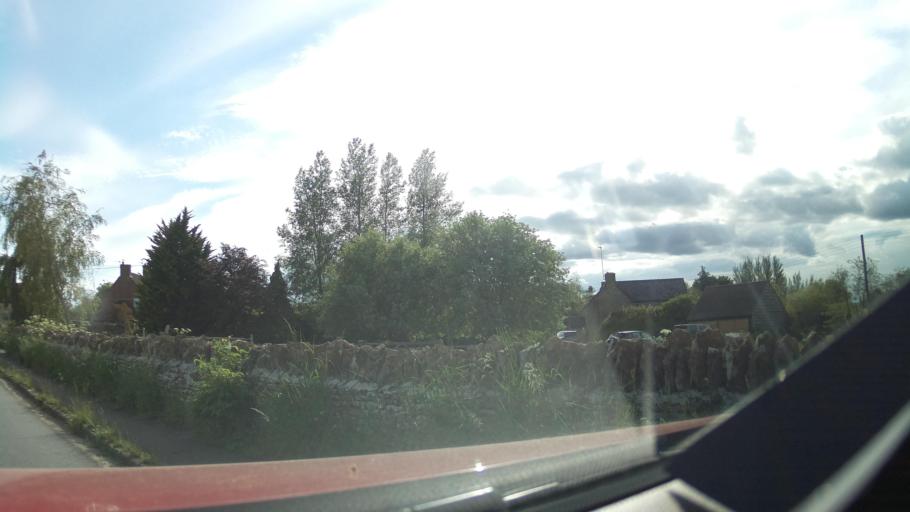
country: GB
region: England
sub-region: Gloucestershire
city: Donnington
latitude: 51.9537
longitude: -1.7773
